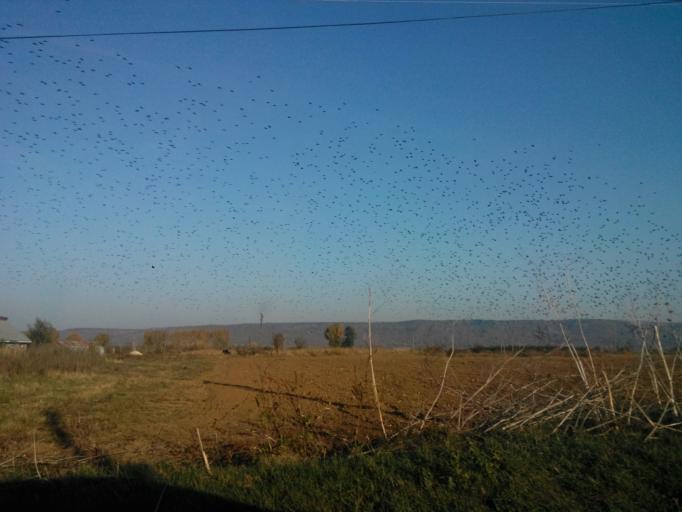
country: RO
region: Vrancea
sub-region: Comuna Pufesti
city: Pufesti
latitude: 46.0185
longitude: 27.1910
